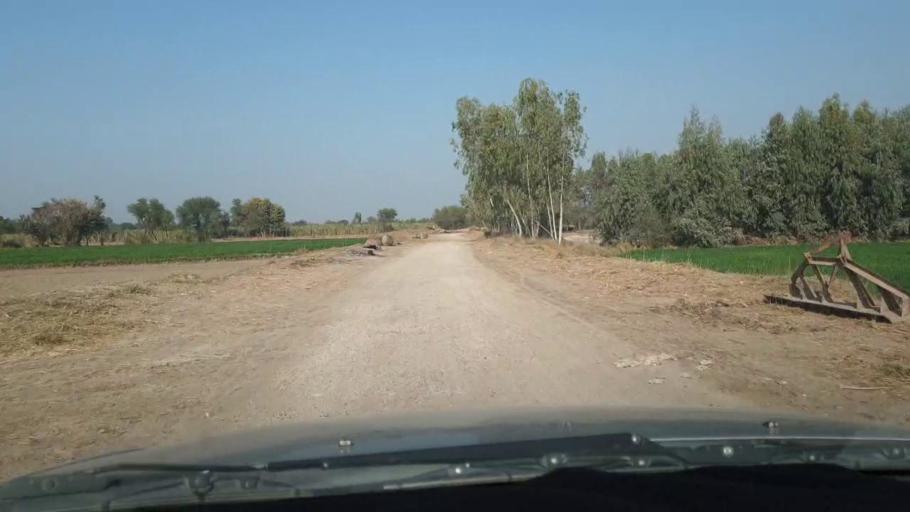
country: PK
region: Sindh
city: Mirpur Mathelo
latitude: 27.9190
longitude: 69.5566
